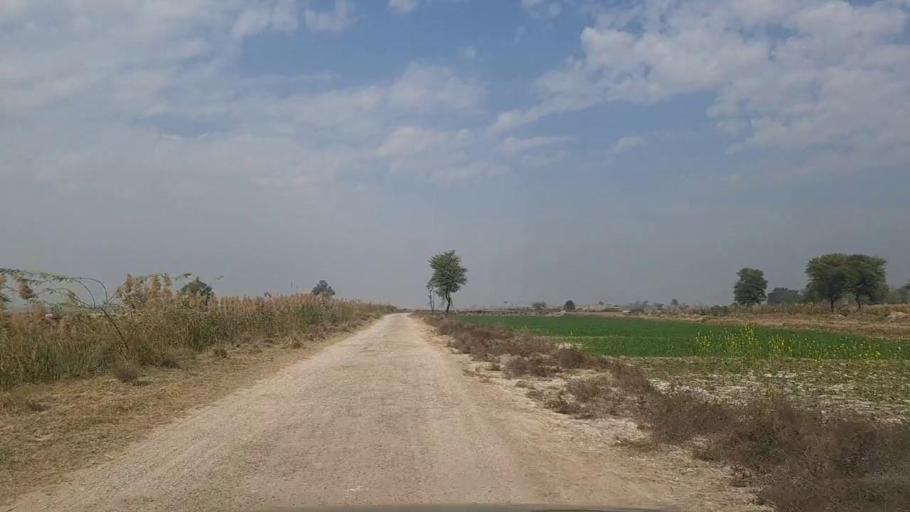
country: PK
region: Sindh
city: Daur
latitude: 26.3971
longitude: 68.3475
